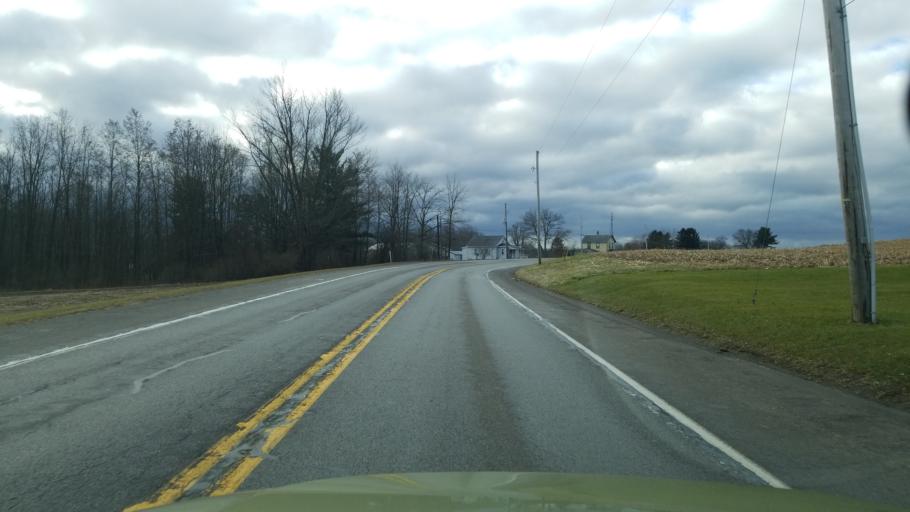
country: US
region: Pennsylvania
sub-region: Jefferson County
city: Punxsutawney
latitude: 40.8555
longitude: -79.0239
